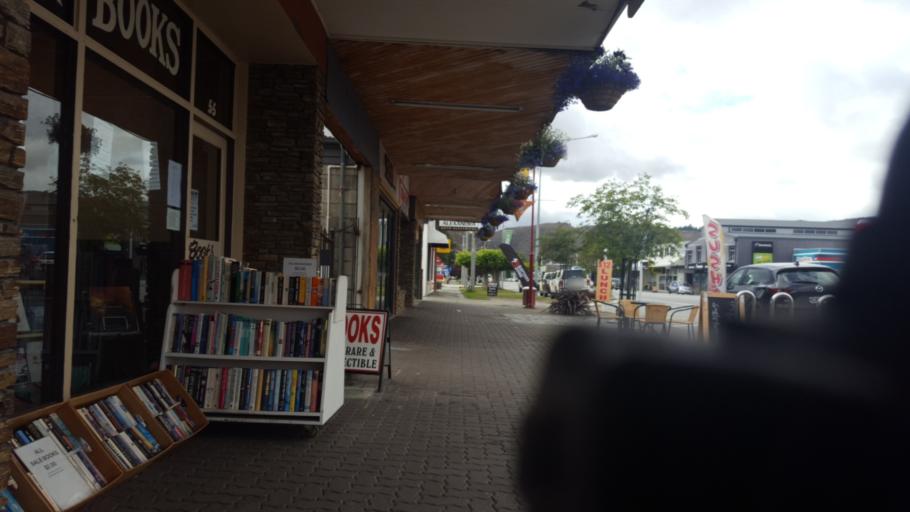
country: NZ
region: Otago
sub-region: Queenstown-Lakes District
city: Wanaka
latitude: -45.2519
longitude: 169.3890
